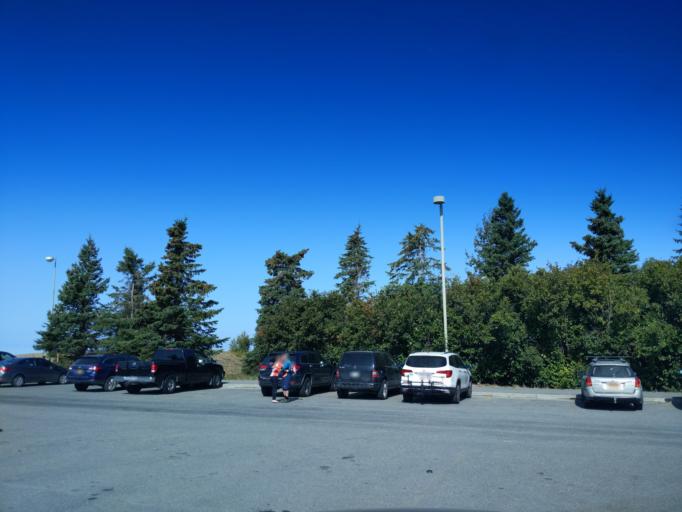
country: US
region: Alaska
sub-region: Anchorage Municipality
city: Anchorage
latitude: 61.1541
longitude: -150.0540
